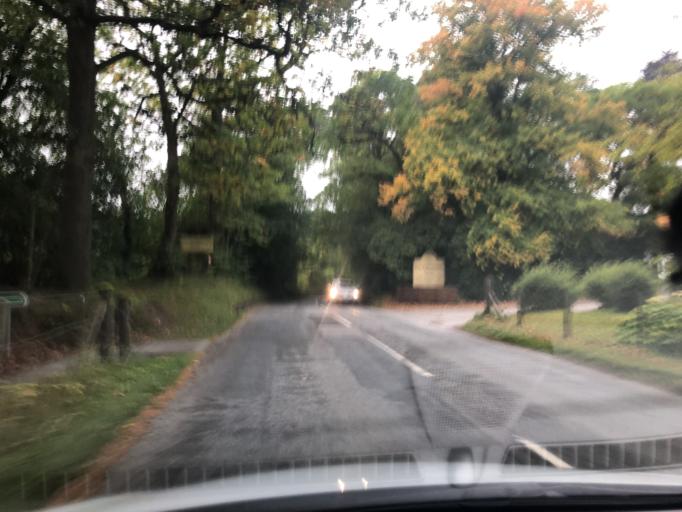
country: GB
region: Scotland
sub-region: Perth and Kinross
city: Pitlochry
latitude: 56.7436
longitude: -3.7757
